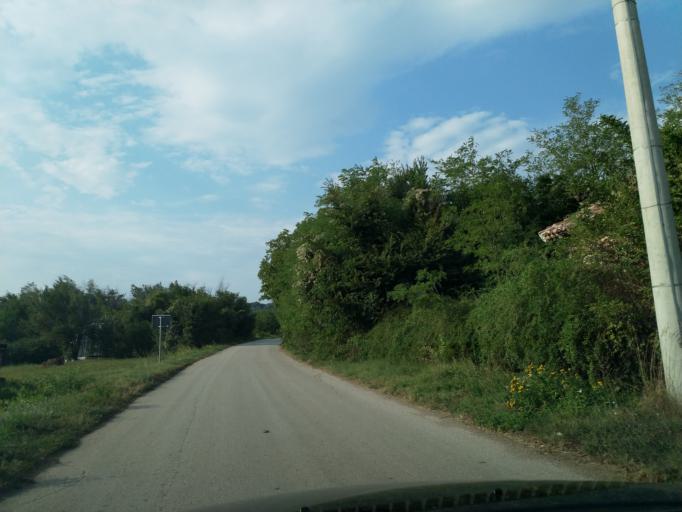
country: RS
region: Central Serbia
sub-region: Pomoravski Okrug
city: Paracin
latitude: 43.8256
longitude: 21.5423
